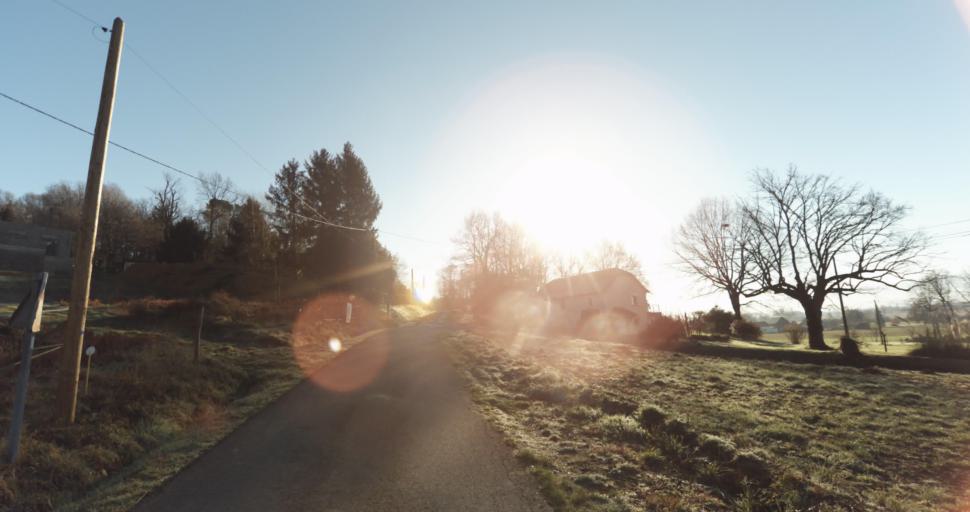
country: FR
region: Aquitaine
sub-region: Departement des Pyrenees-Atlantiques
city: Ousse
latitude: 43.3128
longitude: -0.2460
